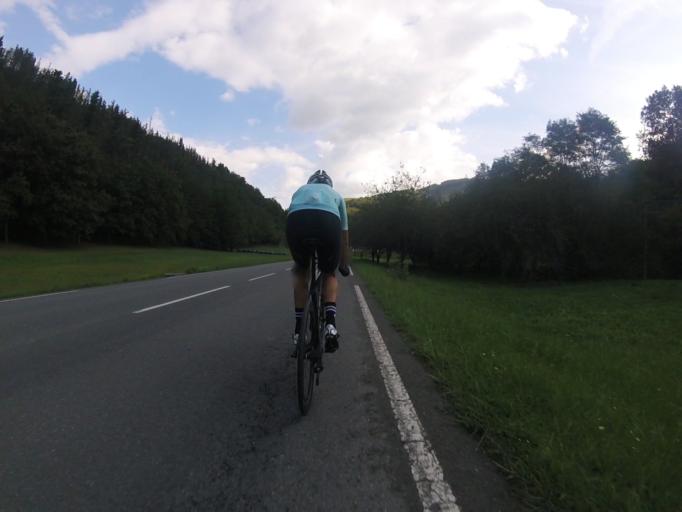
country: ES
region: Basque Country
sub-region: Provincia de Guipuzcoa
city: Amezqueta
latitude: 43.0654
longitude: -2.0861
